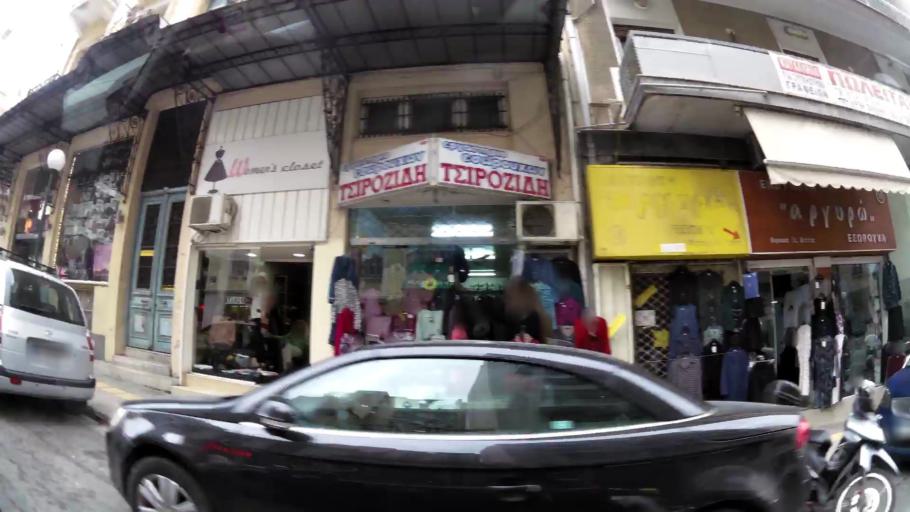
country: GR
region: Attica
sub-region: Nomos Attikis
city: Piraeus
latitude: 37.9452
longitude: 23.6474
